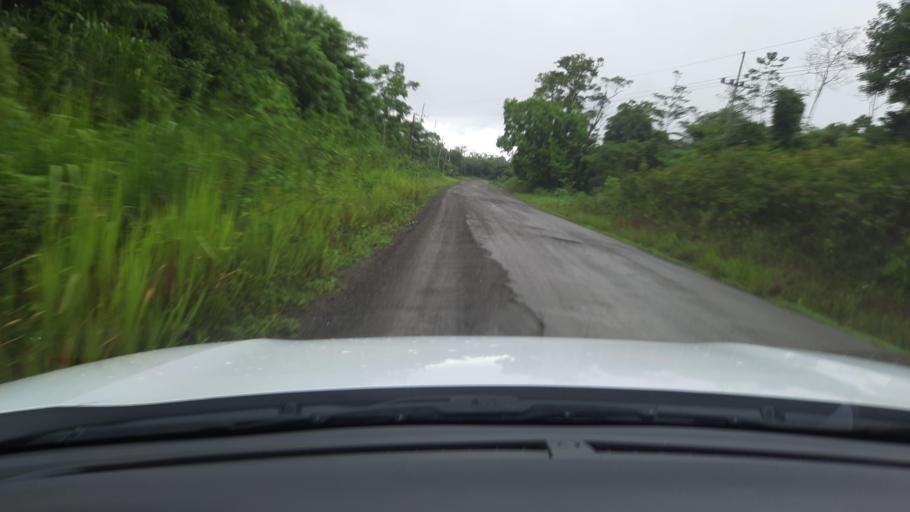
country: CR
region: Alajuela
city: San Jose
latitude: 11.0140
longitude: -85.3307
